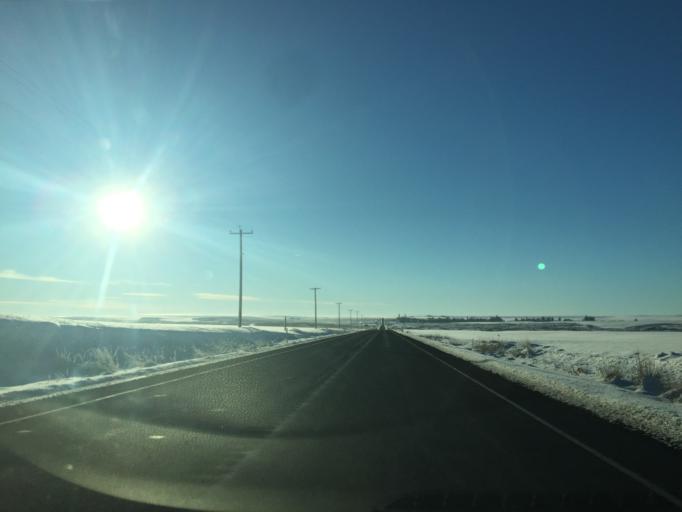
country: US
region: Washington
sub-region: Okanogan County
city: Coulee Dam
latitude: 47.7199
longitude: -118.8990
